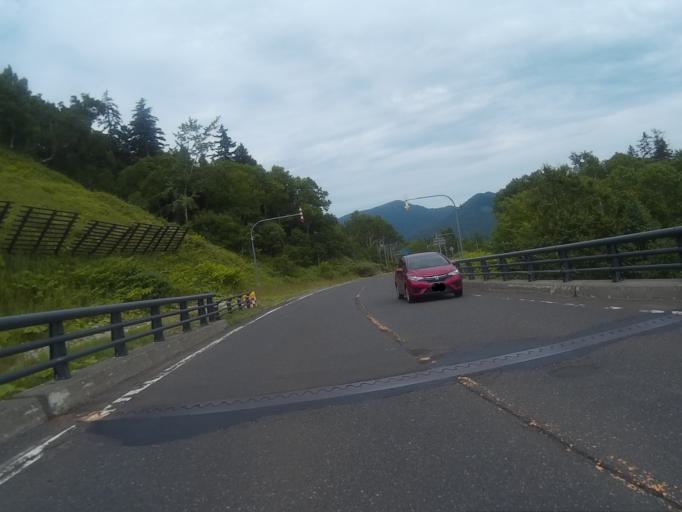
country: JP
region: Hokkaido
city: Sapporo
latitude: 42.8715
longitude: 141.1404
